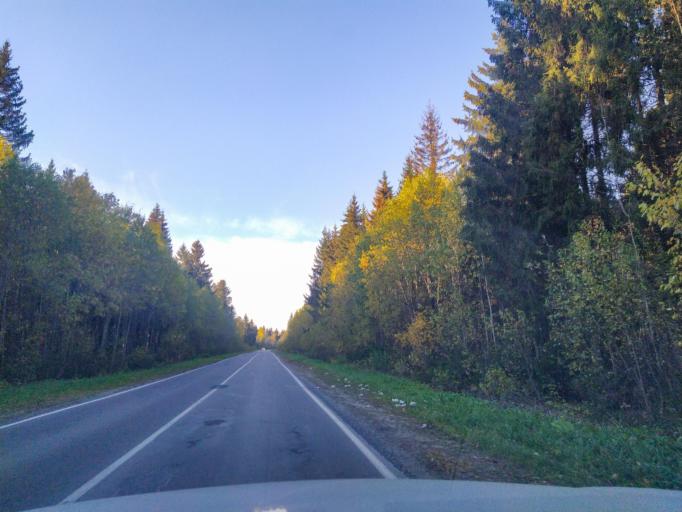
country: RU
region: Leningrad
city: Siverskiy
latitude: 59.3050
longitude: 30.0331
